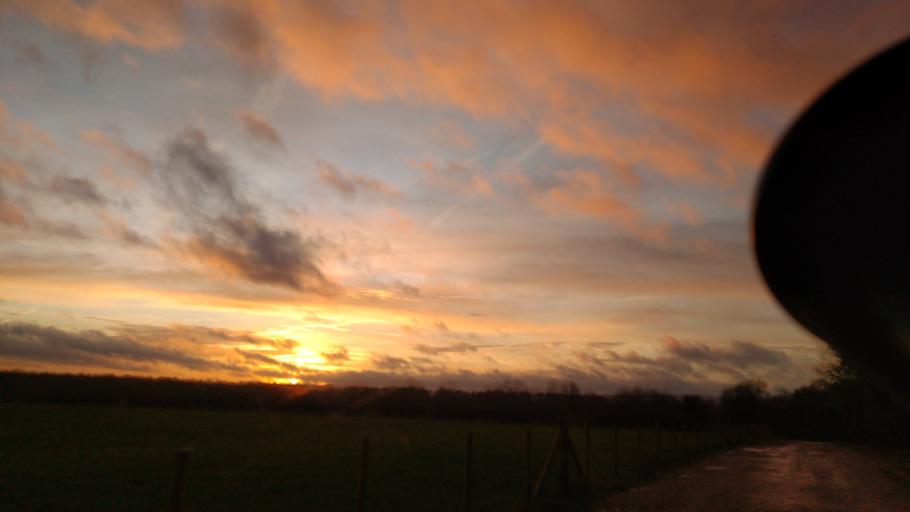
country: GB
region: England
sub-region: Borough of Swindon
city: Highworth
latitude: 51.5926
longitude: -1.6954
